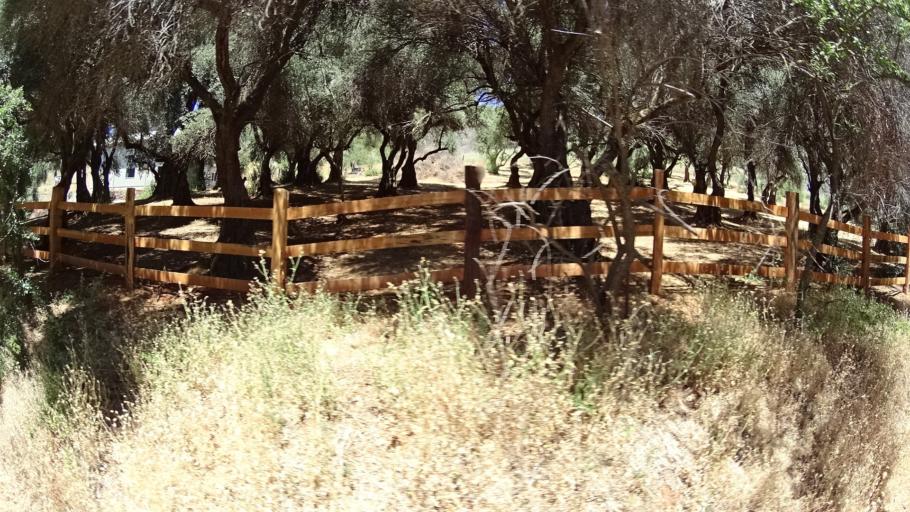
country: US
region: California
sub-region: Calaveras County
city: San Andreas
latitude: 38.2853
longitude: -120.6304
